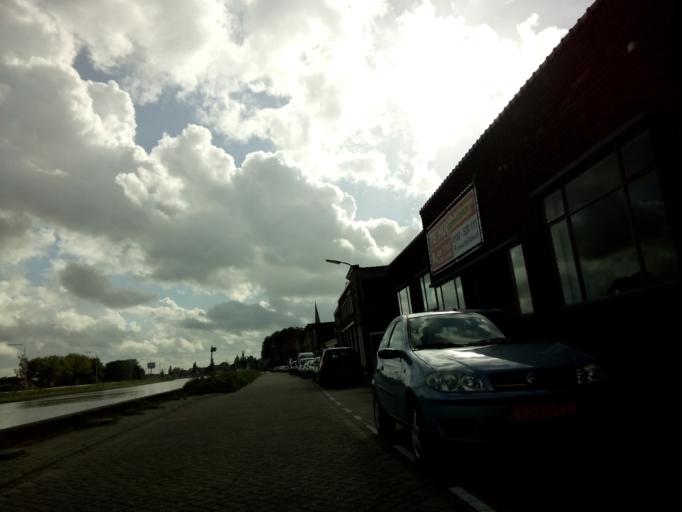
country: NL
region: South Holland
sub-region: Gemeente Waddinxveen
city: Waddinxveen
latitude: 52.0344
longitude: 4.6585
